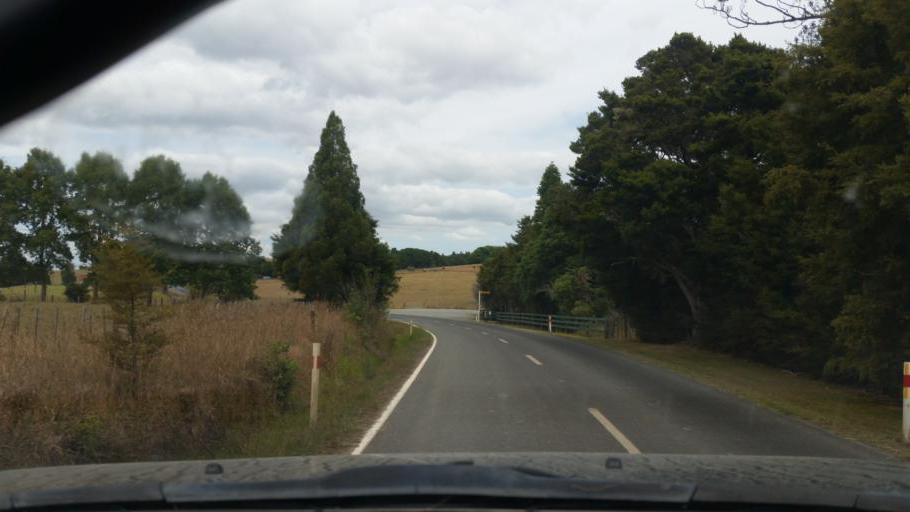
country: NZ
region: Northland
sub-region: Kaipara District
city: Dargaville
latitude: -35.7206
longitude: 173.6525
